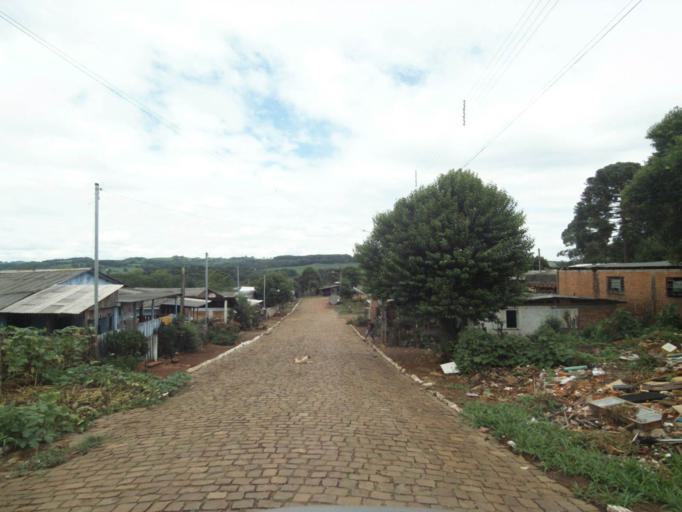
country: BR
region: Rio Grande do Sul
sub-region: Lagoa Vermelha
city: Lagoa Vermelha
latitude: -28.2249
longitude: -51.5397
